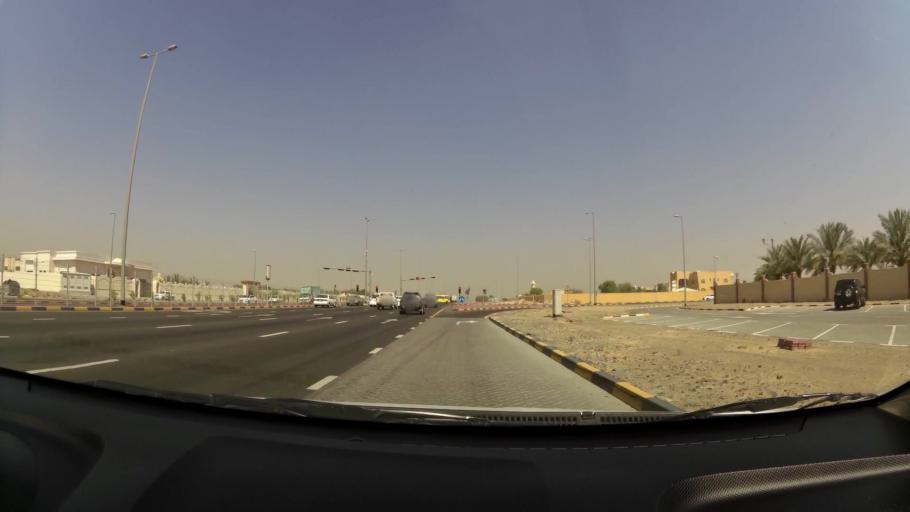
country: AE
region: Ajman
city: Ajman
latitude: 25.3894
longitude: 55.5474
